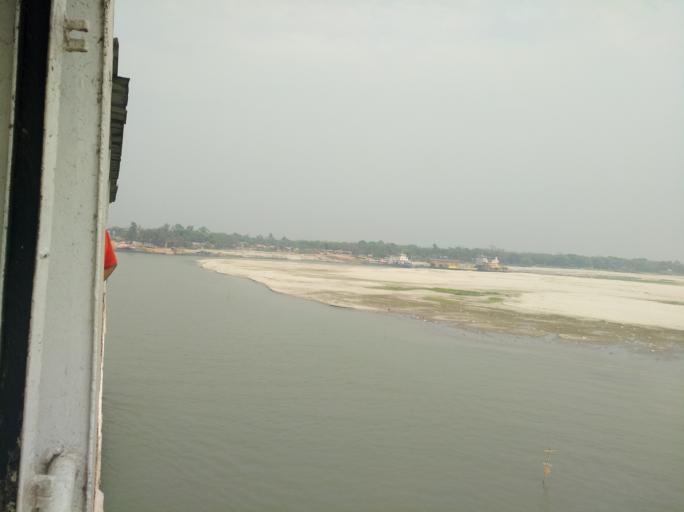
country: BD
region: Dhaka
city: Faridpur
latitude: 23.7826
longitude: 89.8091
